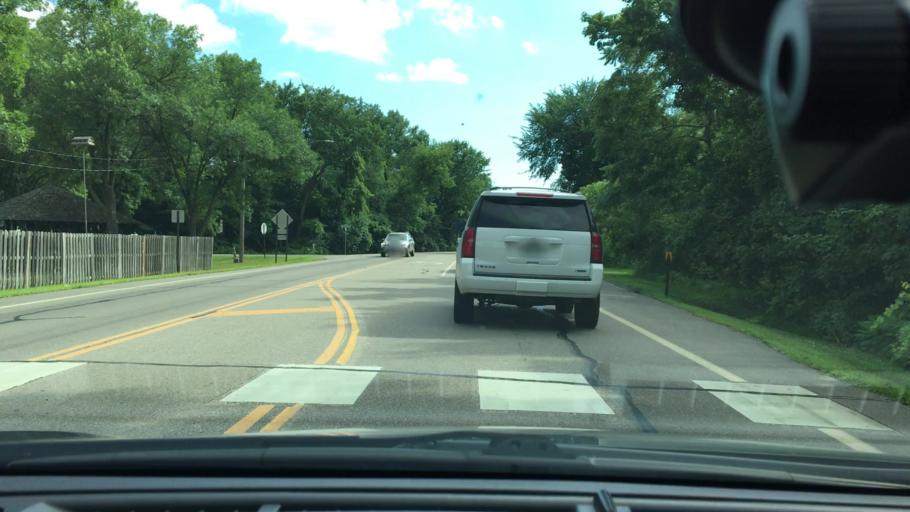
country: US
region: Minnesota
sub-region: Hennepin County
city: Tonka Bay
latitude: 44.9373
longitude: -93.6020
